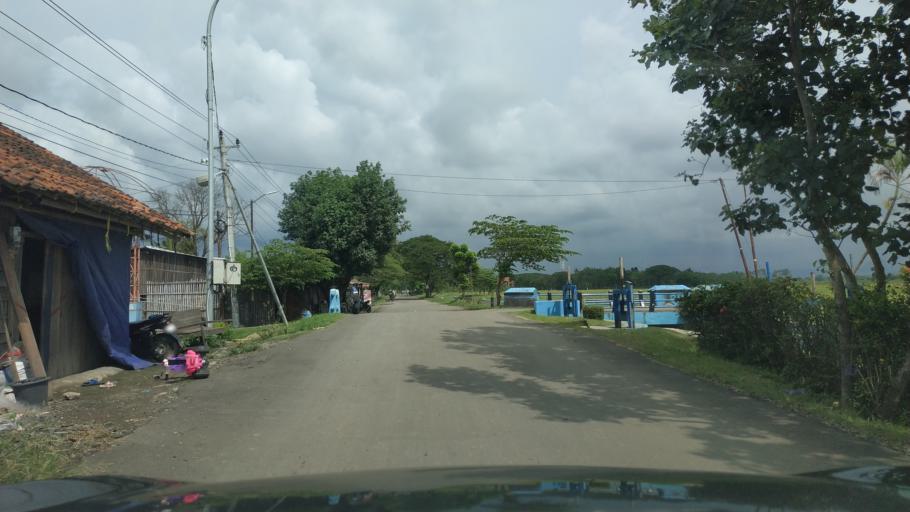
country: ID
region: Central Java
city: Pemalang
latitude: -6.9069
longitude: 109.3271
